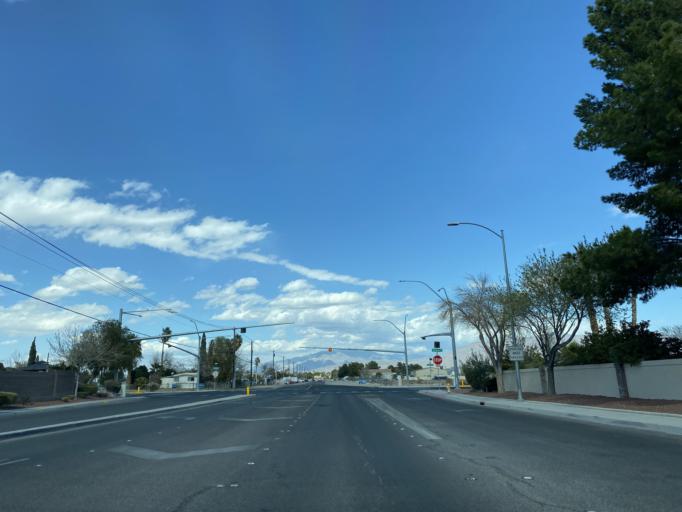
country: US
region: Nevada
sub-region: Clark County
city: Spring Valley
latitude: 36.2471
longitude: -115.2603
